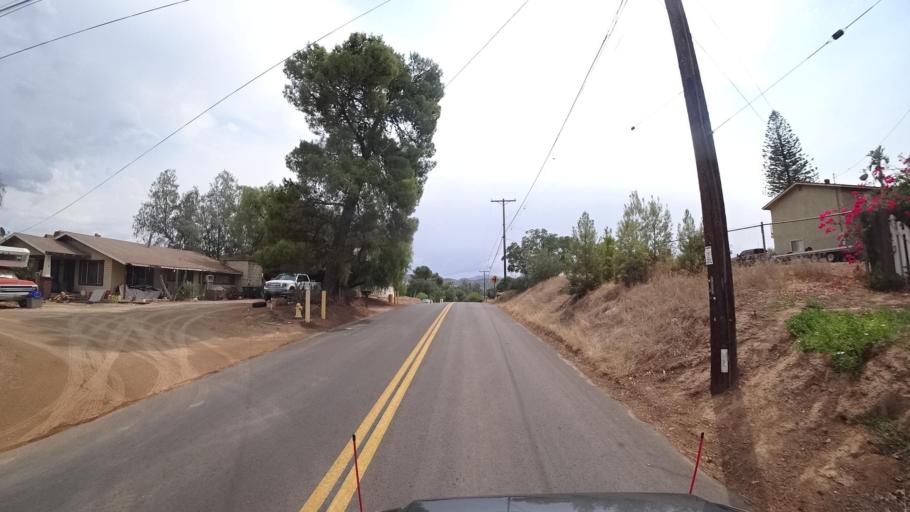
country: US
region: California
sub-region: San Diego County
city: Ramona
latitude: 33.0380
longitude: -116.8588
